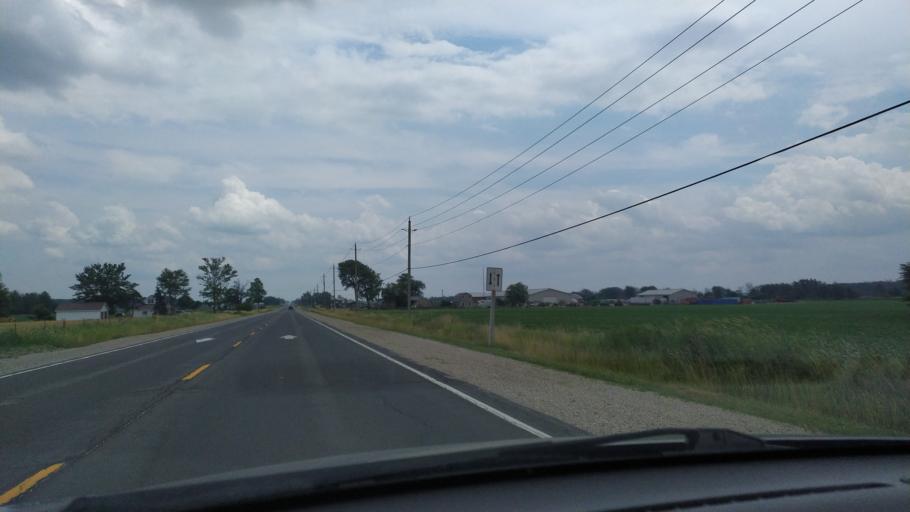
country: CA
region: Ontario
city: Stratford
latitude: 43.3702
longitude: -80.9049
